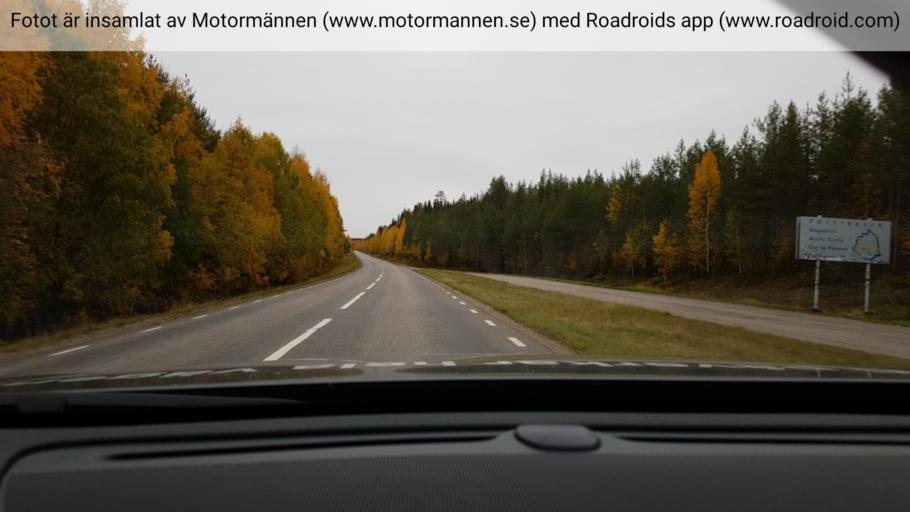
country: SE
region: Norrbotten
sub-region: Overkalix Kommun
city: OEverkalix
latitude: 66.5525
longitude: 22.7591
